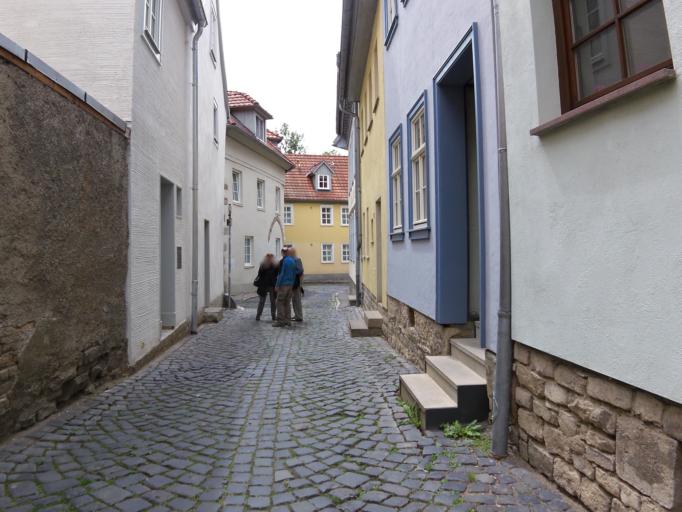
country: DE
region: Thuringia
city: Erfurt
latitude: 50.9805
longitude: 11.0302
